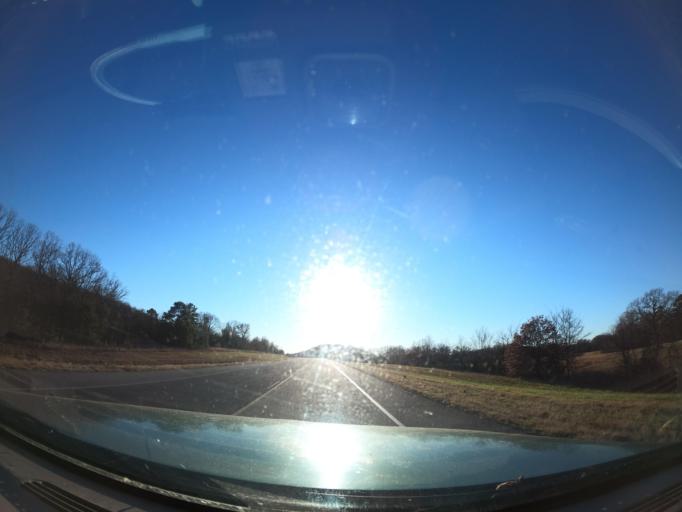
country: US
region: Oklahoma
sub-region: Pittsburg County
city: Hartshorne
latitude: 34.8647
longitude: -95.5251
